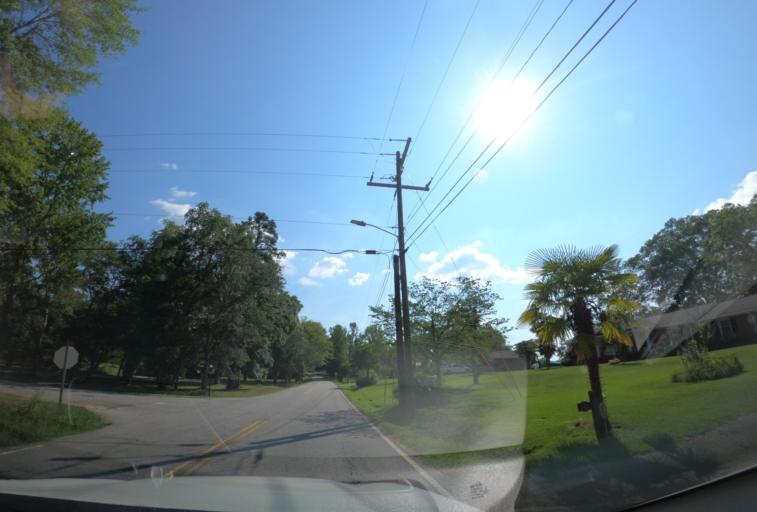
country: US
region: South Carolina
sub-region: Anderson County
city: Belton
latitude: 34.5220
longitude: -82.5120
